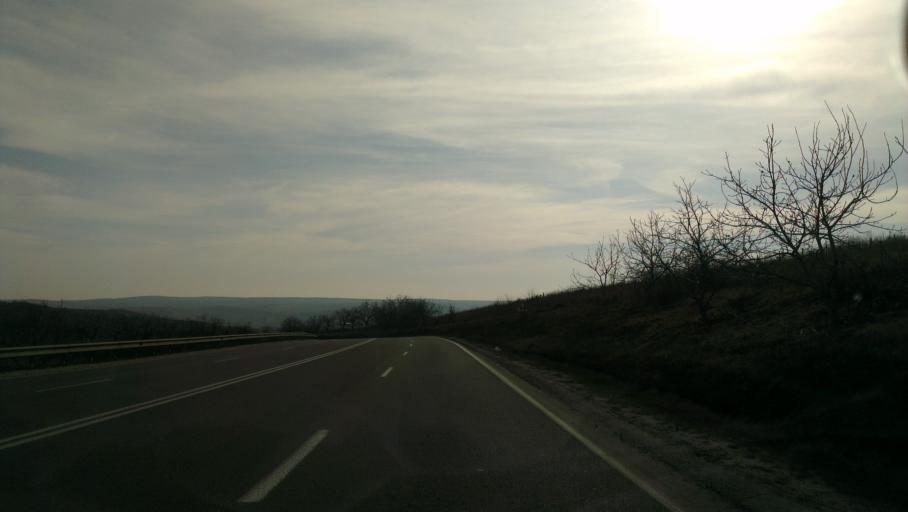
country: MD
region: Laloveni
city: Ialoveni
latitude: 46.9406
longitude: 28.7045
